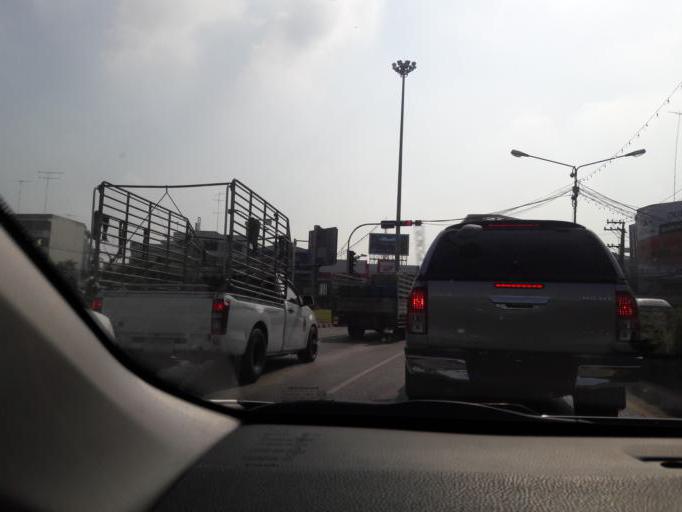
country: TH
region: Ang Thong
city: Ang Thong
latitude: 14.5936
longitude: 100.4514
